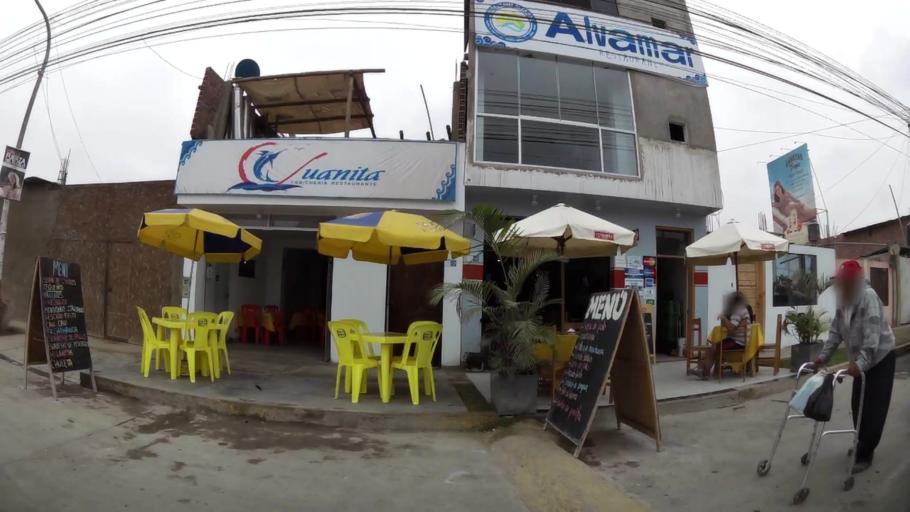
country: PE
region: Lima
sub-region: Lima
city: Punta Hermosa
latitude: -12.3096
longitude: -76.8370
